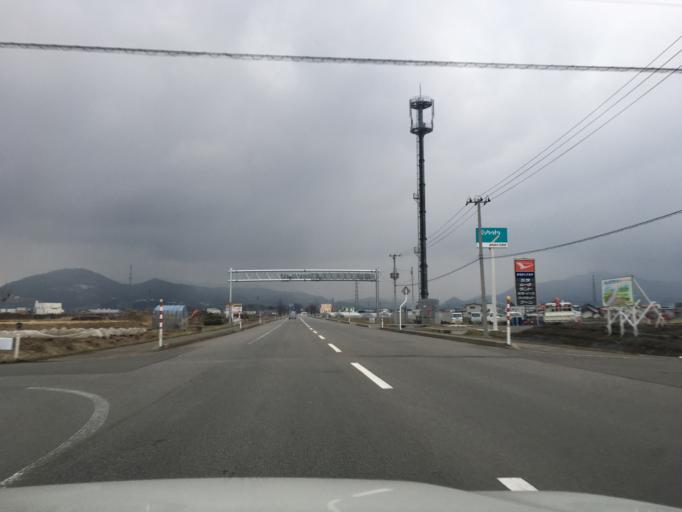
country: JP
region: Aomori
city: Kuroishi
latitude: 40.5798
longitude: 140.5685
